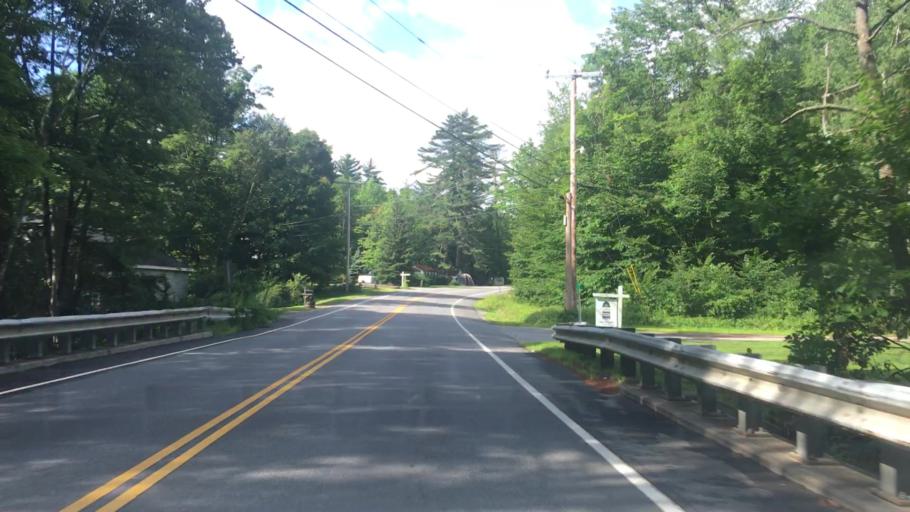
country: US
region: New Hampshire
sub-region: Belknap County
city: Gilford
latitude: 43.5540
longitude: -71.4010
